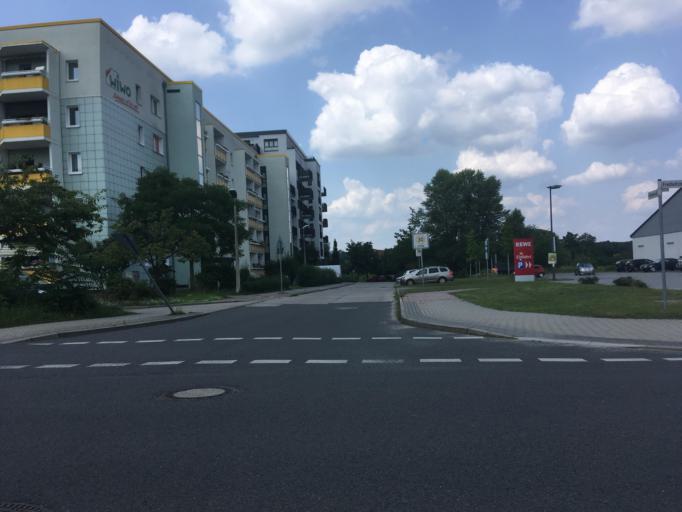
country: DE
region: Brandenburg
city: Wildau
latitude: 52.3247
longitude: 13.6233
